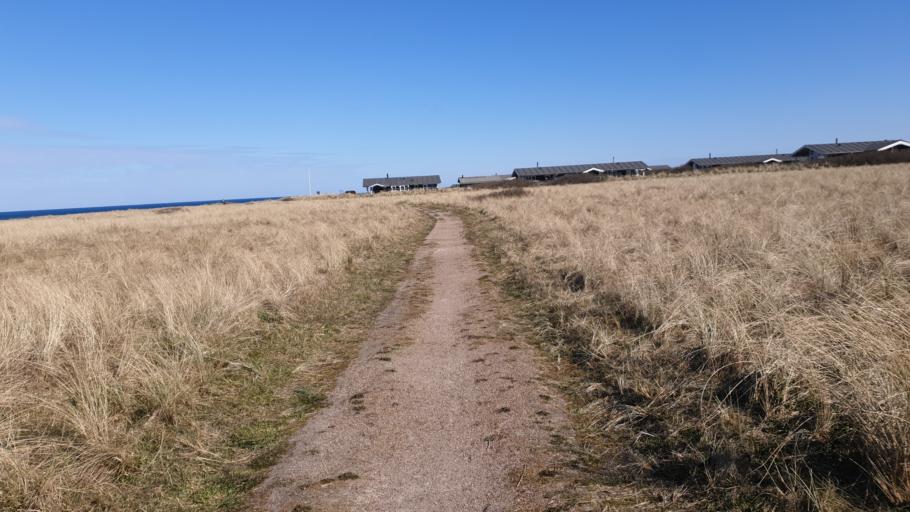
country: DK
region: North Denmark
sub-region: Hjorring Kommune
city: Hjorring
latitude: 57.4931
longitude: 9.8315
